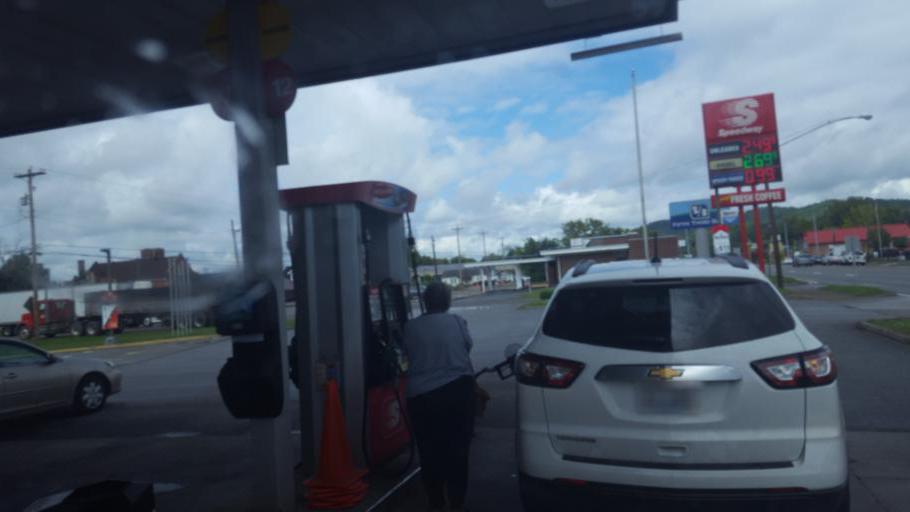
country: US
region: Ohio
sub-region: Scioto County
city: Lucasville
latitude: 38.8782
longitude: -82.9971
